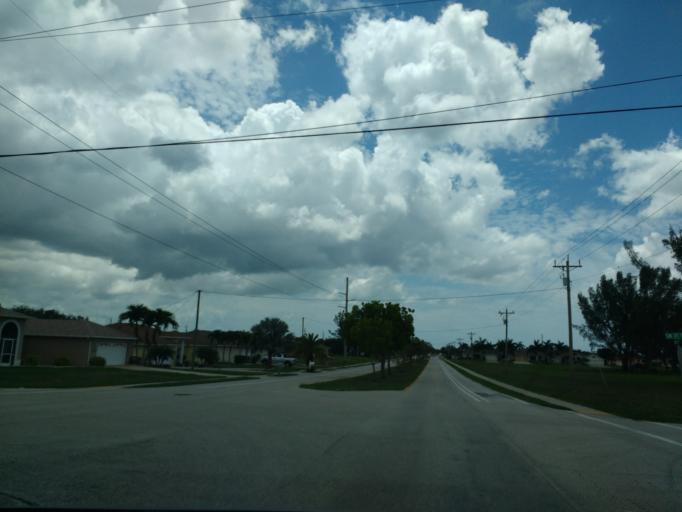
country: US
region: Florida
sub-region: Lee County
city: Cape Coral
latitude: 26.5673
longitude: -82.0174
